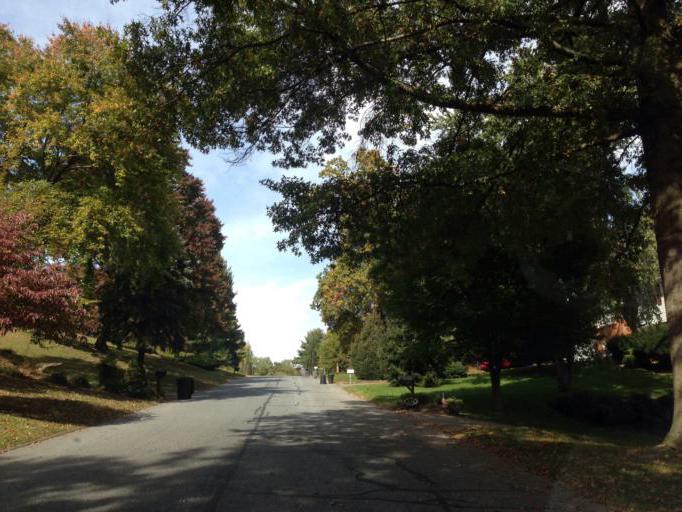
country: US
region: Maryland
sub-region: Howard County
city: Columbia
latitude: 39.2841
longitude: -76.8495
